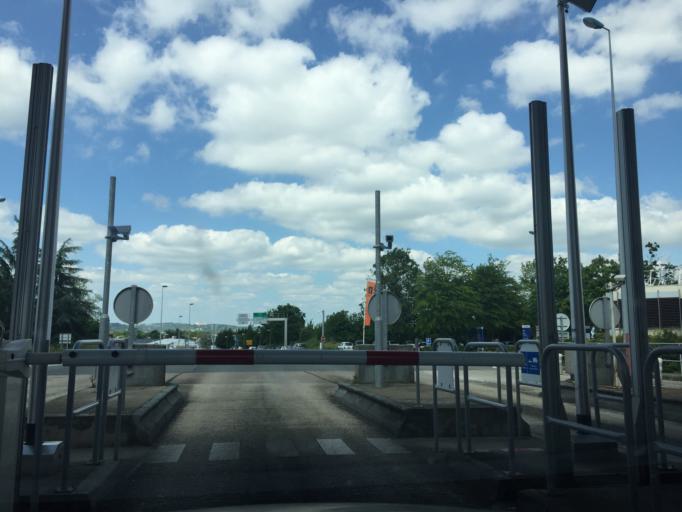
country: FR
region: Aquitaine
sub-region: Departement du Lot-et-Garonne
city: Boe
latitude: 44.1650
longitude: 0.6057
